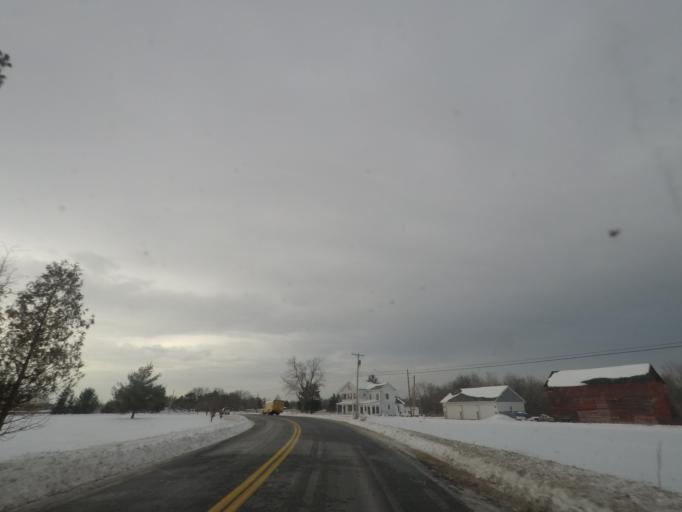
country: US
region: New York
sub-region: Rensselaer County
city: Castleton-on-Hudson
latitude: 42.5079
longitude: -73.7466
